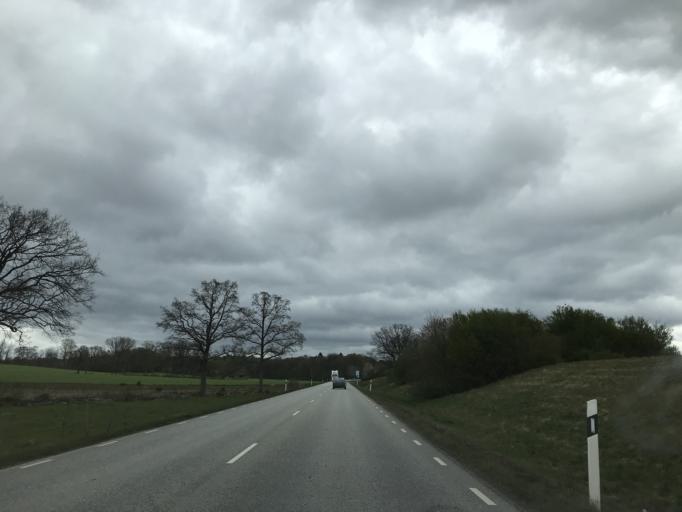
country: SE
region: Skane
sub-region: Hoors Kommun
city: Hoeoer
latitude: 55.9431
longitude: 13.5284
